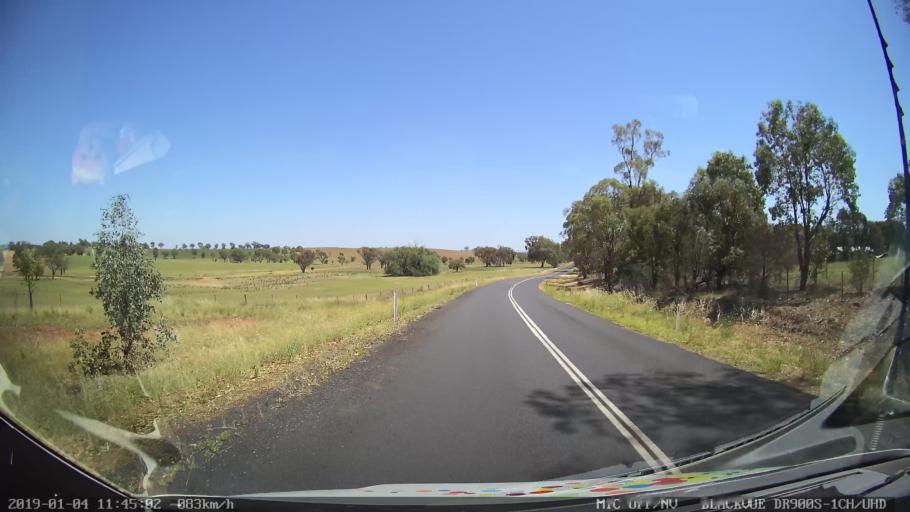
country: AU
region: New South Wales
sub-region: Cabonne
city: Molong
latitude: -32.9587
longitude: 148.7652
